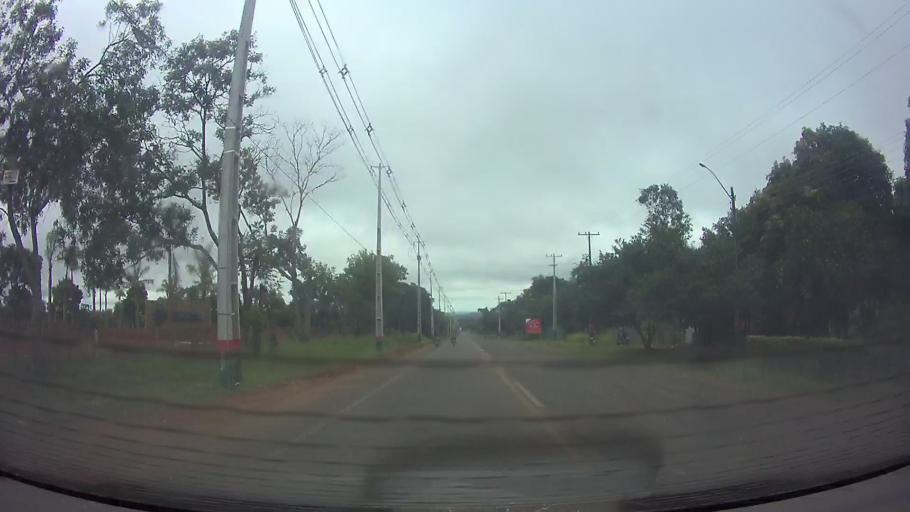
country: PY
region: Cordillera
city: Altos
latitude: -25.2737
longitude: -57.2599
